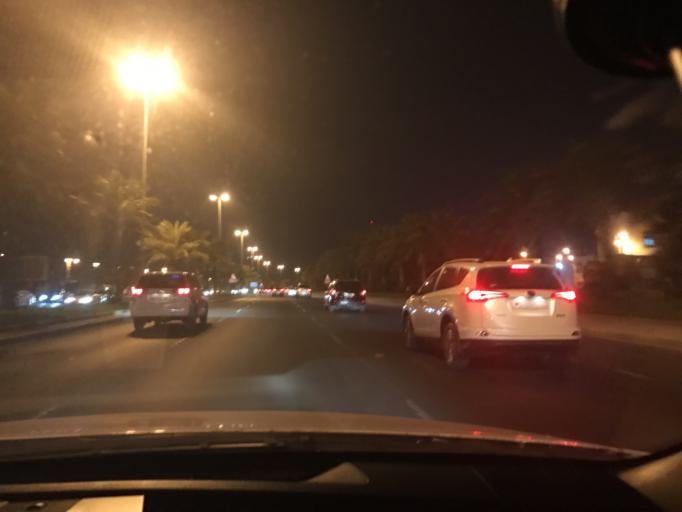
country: BH
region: Muharraq
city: Al Muharraq
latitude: 26.2485
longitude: 50.6196
